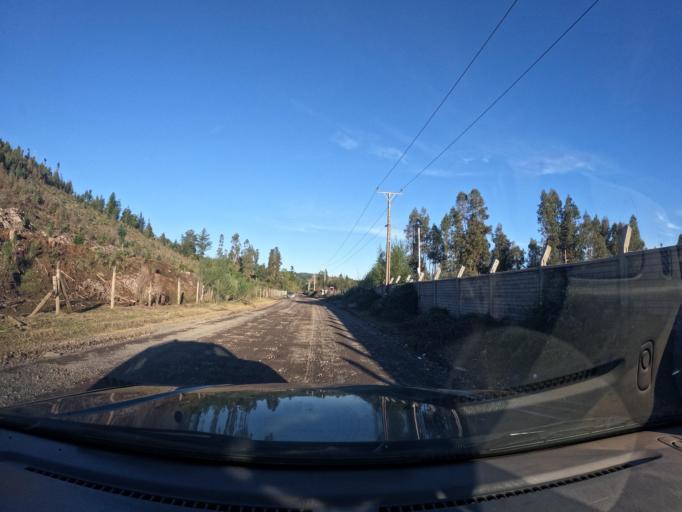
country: CL
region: Biobio
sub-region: Provincia de Concepcion
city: Chiguayante
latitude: -37.0764
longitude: -72.9414
